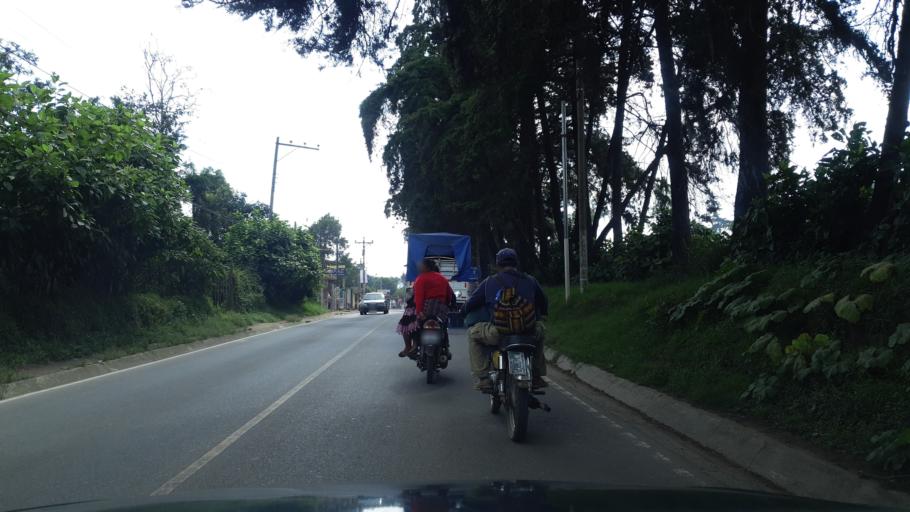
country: GT
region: Chimaltenango
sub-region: Municipio de Chimaltenango
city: Chimaltenango
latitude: 14.6653
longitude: -90.8086
